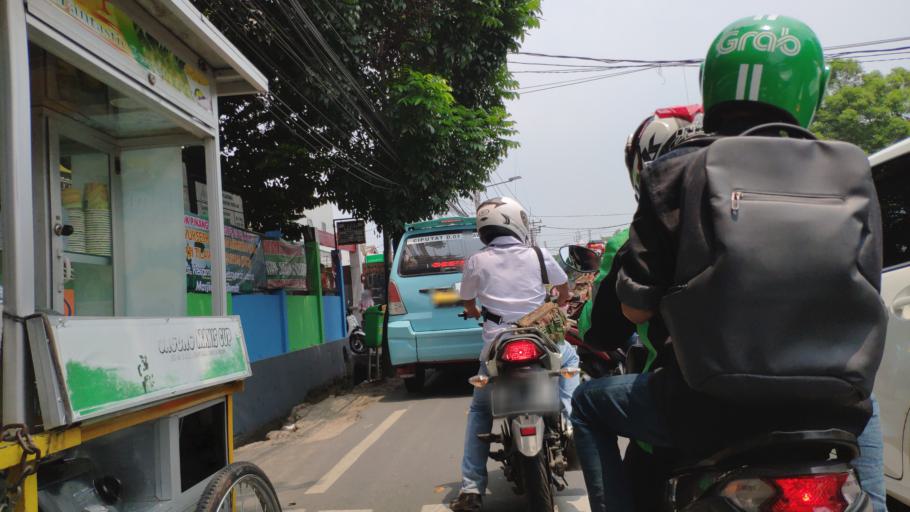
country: ID
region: Banten
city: South Tangerang
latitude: -6.2698
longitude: 106.7750
